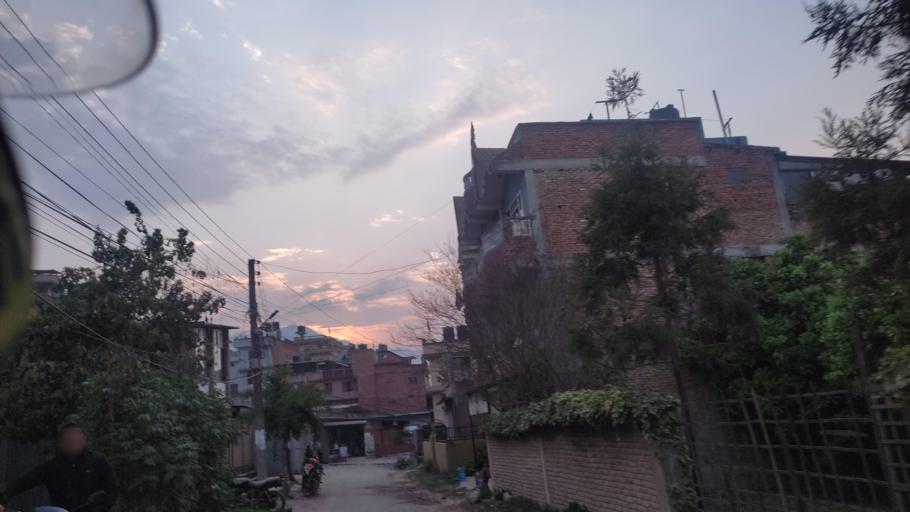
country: NP
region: Central Region
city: Kirtipur
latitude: 27.6723
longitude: 85.2805
